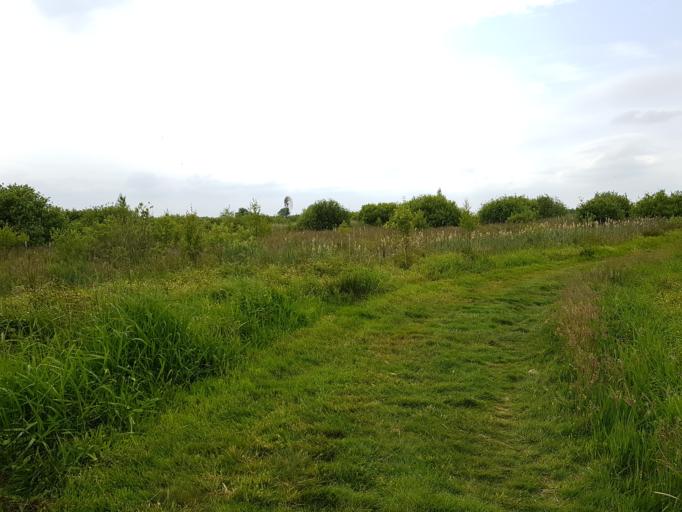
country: NL
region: Friesland
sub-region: Gemeente Tytsjerksteradiel
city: Garyp
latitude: 53.1439
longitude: 5.9433
